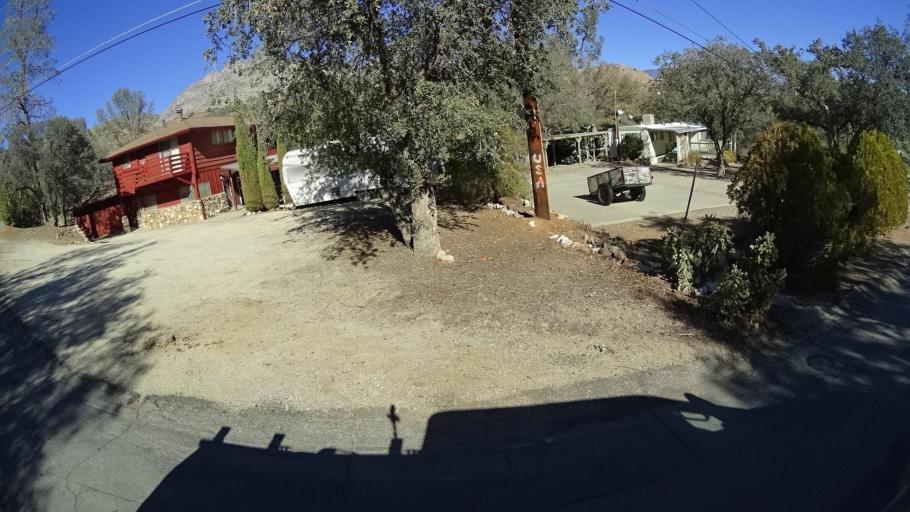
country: US
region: California
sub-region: Kern County
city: Wofford Heights
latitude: 35.7066
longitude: -118.4675
